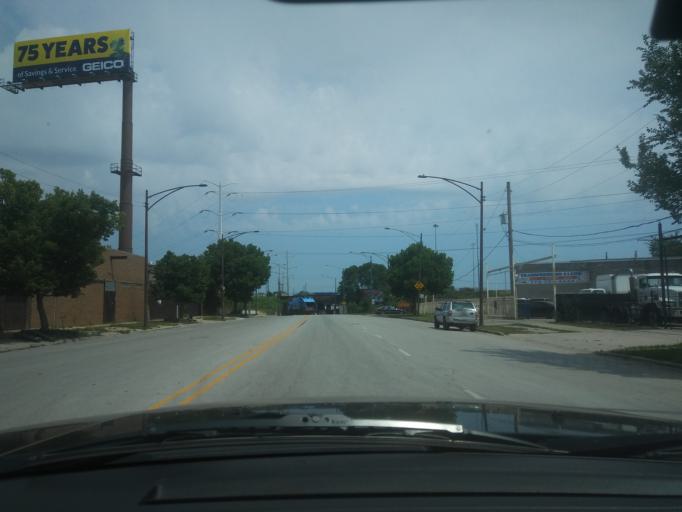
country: US
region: Illinois
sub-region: Cook County
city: Chicago
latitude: 41.7766
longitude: -87.6252
